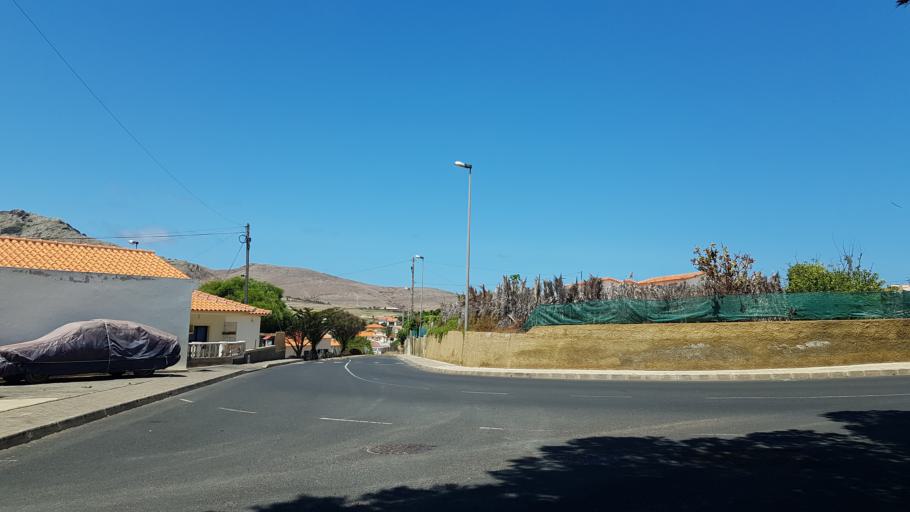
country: PT
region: Madeira
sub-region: Porto Santo
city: Vila de Porto Santo
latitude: 33.0547
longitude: -16.3557
